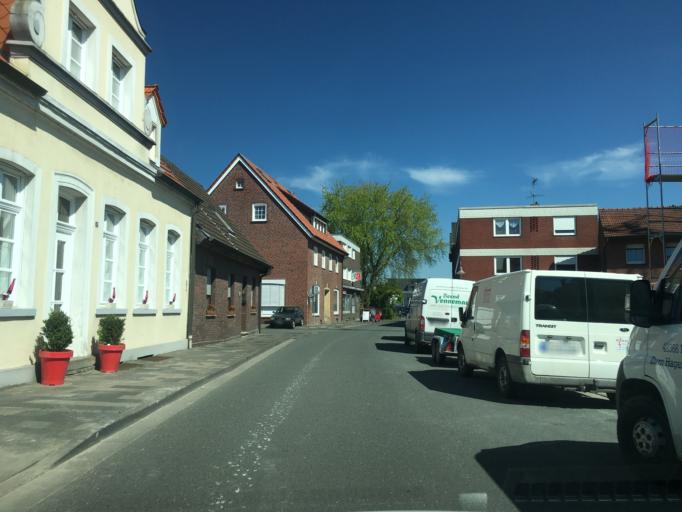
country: DE
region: North Rhine-Westphalia
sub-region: Regierungsbezirk Munster
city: Laer
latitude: 52.0558
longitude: 7.3564
